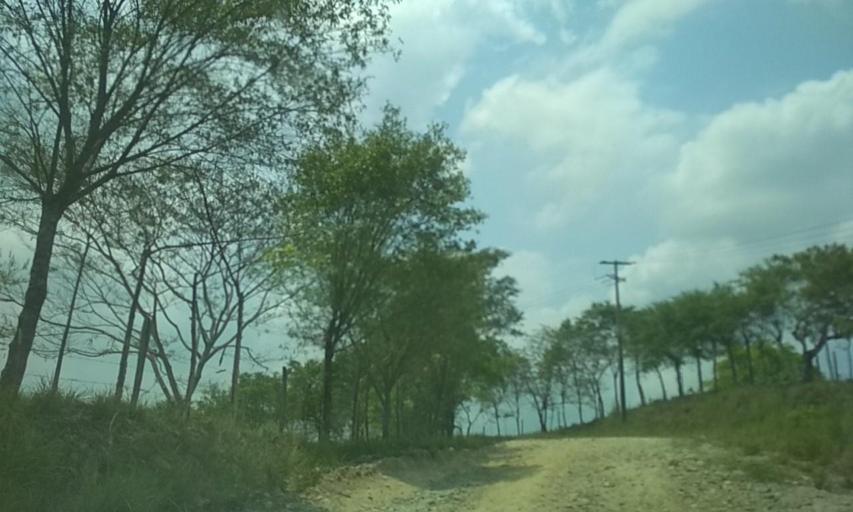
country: MX
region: Tabasco
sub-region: Huimanguillo
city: Francisco Rueda
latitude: 17.6103
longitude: -93.8088
